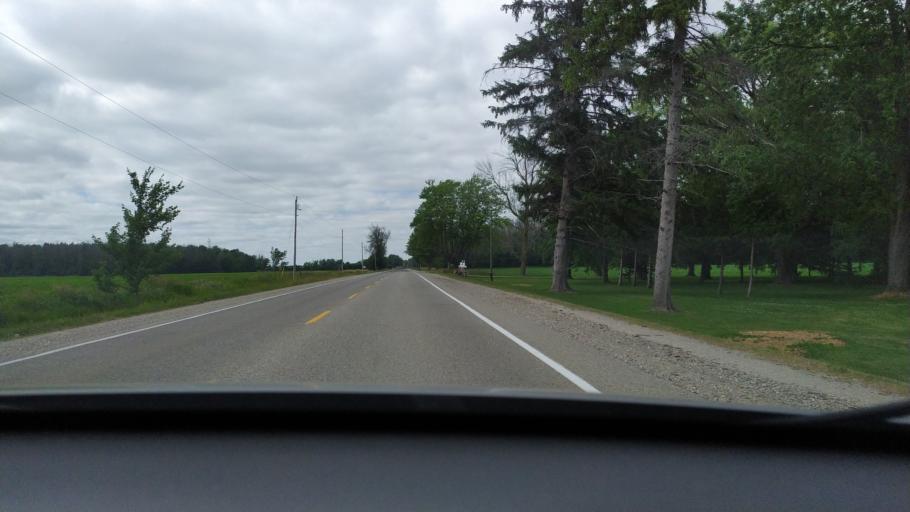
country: CA
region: Ontario
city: Stratford
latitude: 43.3372
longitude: -80.9634
